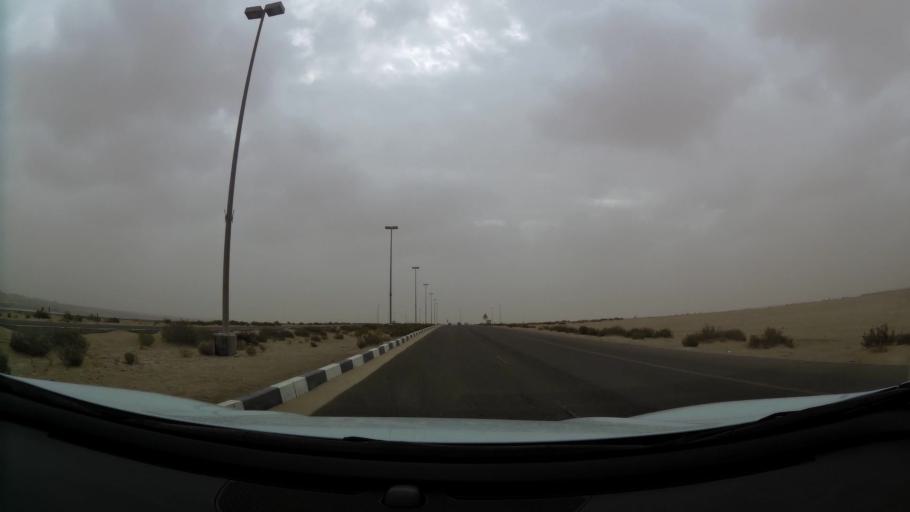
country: AE
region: Abu Dhabi
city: Abu Dhabi
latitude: 24.4625
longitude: 54.6865
